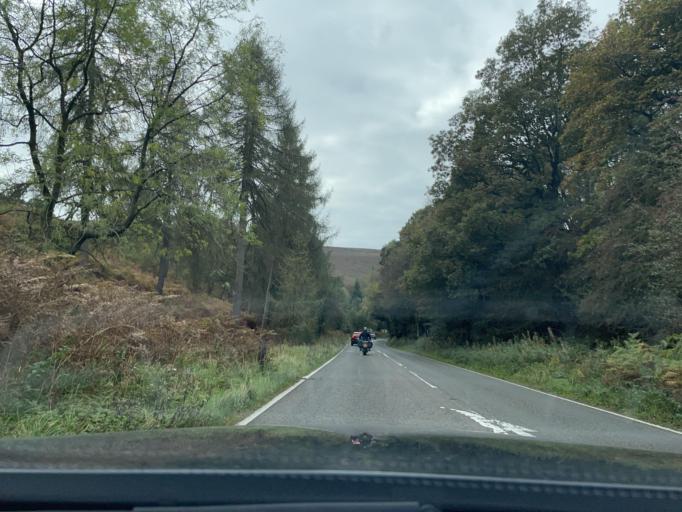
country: GB
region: England
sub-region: Derbyshire
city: Hathersage
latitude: 53.3796
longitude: -1.6832
